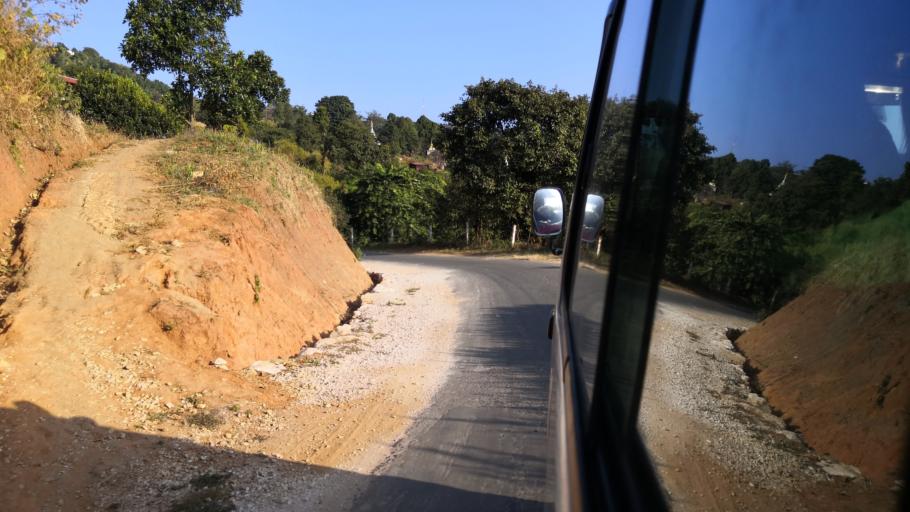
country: MM
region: Mandalay
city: Mogok
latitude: 22.9048
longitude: 96.3868
